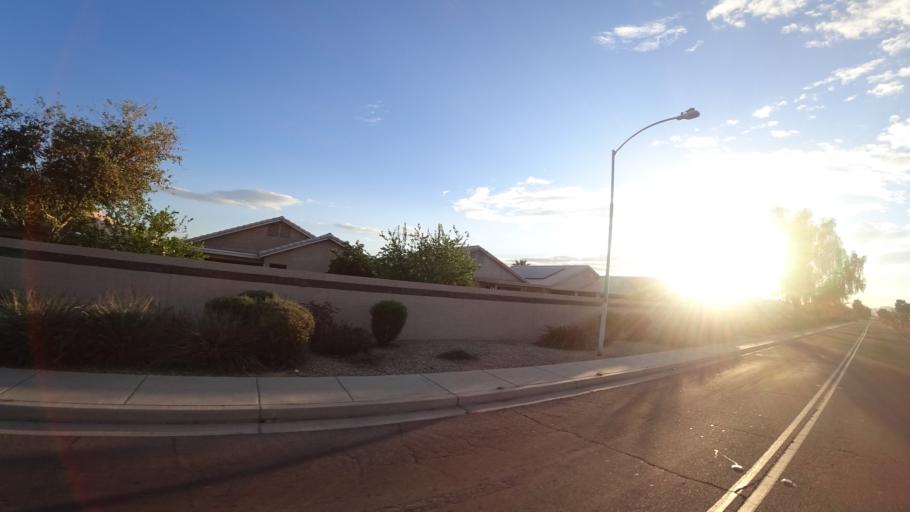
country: US
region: Arizona
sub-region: Maricopa County
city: Glendale
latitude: 33.5454
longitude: -112.2085
